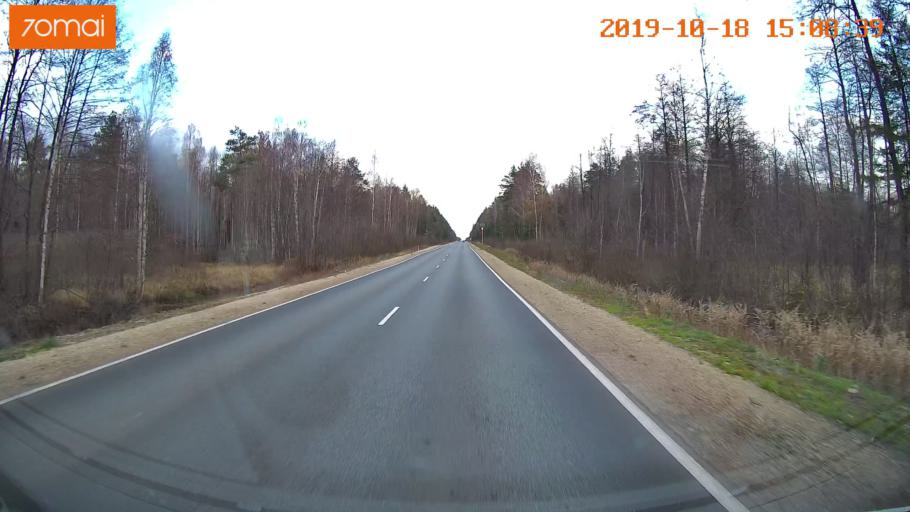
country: RU
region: Vladimir
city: Gus'-Khrustal'nyy
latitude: 55.5552
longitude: 40.6127
